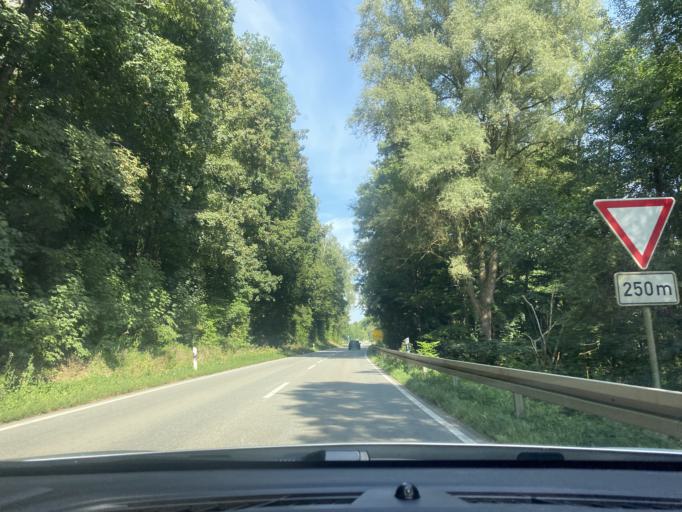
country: DE
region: Bavaria
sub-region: Upper Bavaria
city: Haag an der Amper
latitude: 48.4604
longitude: 11.8467
